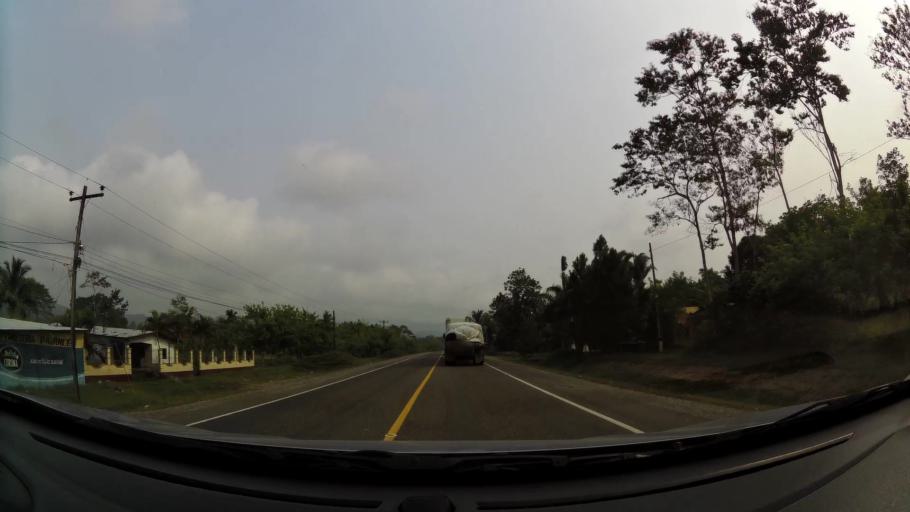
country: HN
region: Atlantida
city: Mezapa
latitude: 15.6193
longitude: -87.6162
